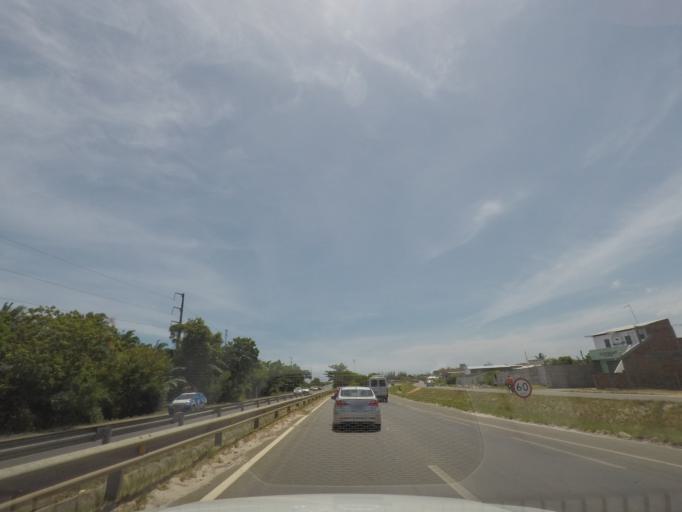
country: BR
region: Bahia
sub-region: Mata De Sao Joao
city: Mata de Sao Joao
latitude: -12.5973
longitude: -38.0440
